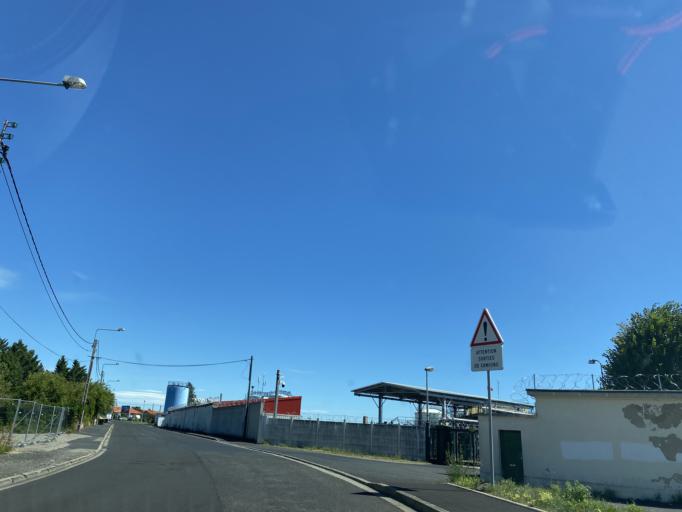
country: FR
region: Auvergne
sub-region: Departement du Puy-de-Dome
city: Le Cendre
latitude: 45.7369
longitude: 3.1718
